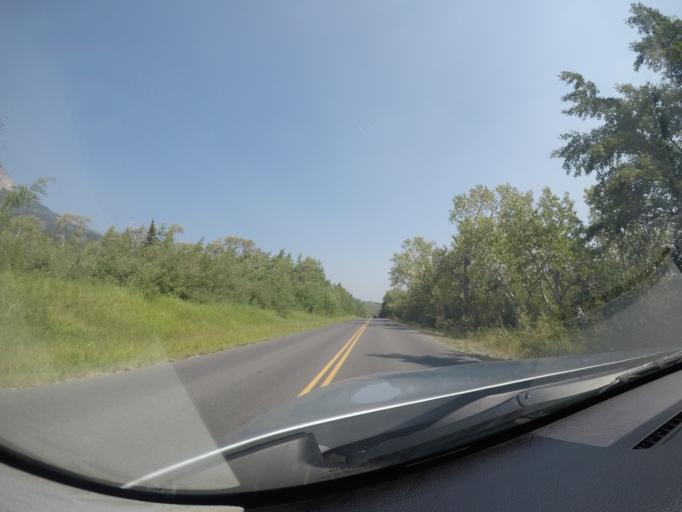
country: US
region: Montana
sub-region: Glacier County
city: North Browning
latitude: 48.7328
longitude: -113.4615
